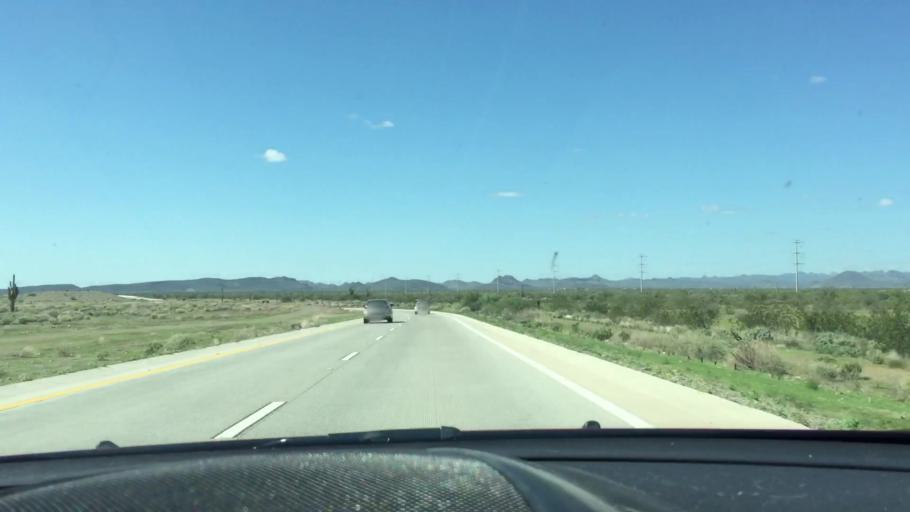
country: US
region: Arizona
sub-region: Maricopa County
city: Anthem
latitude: 33.7825
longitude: -112.1971
